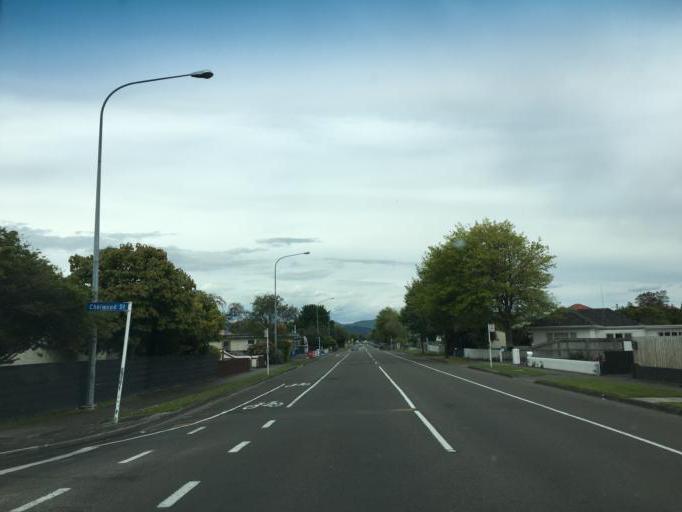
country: NZ
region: Manawatu-Wanganui
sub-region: Palmerston North City
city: Palmerston North
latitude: -40.3599
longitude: 175.5917
